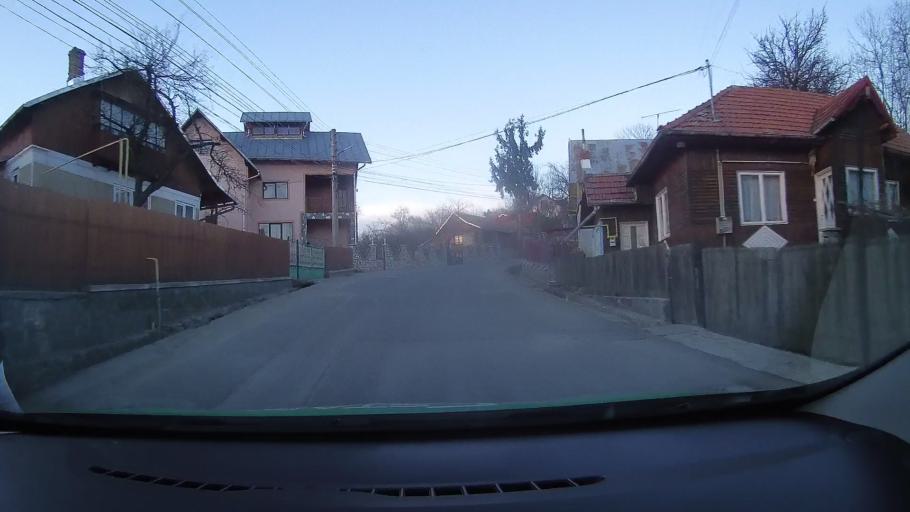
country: RO
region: Prahova
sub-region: Comuna Comarnic
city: Comarnic
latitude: 45.2494
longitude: 25.6429
